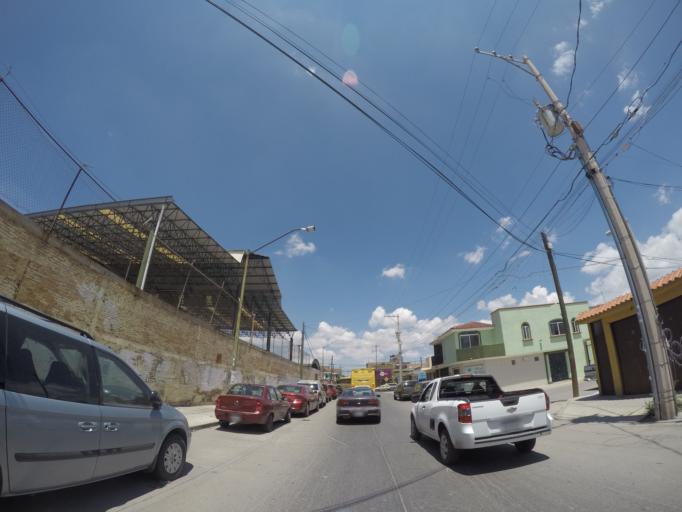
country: MX
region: San Luis Potosi
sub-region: San Luis Potosi
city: San Luis Potosi
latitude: 22.1545
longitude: -100.9586
